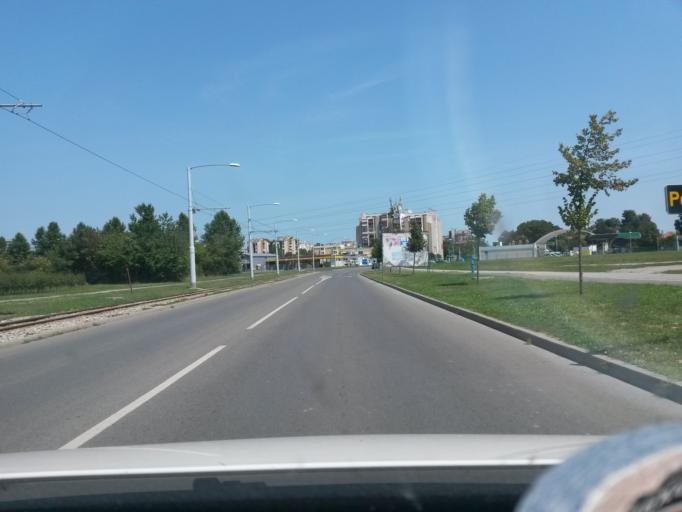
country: HR
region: Osjecko-Baranjska
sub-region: Grad Osijek
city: Osijek
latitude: 45.5479
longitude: 18.6897
